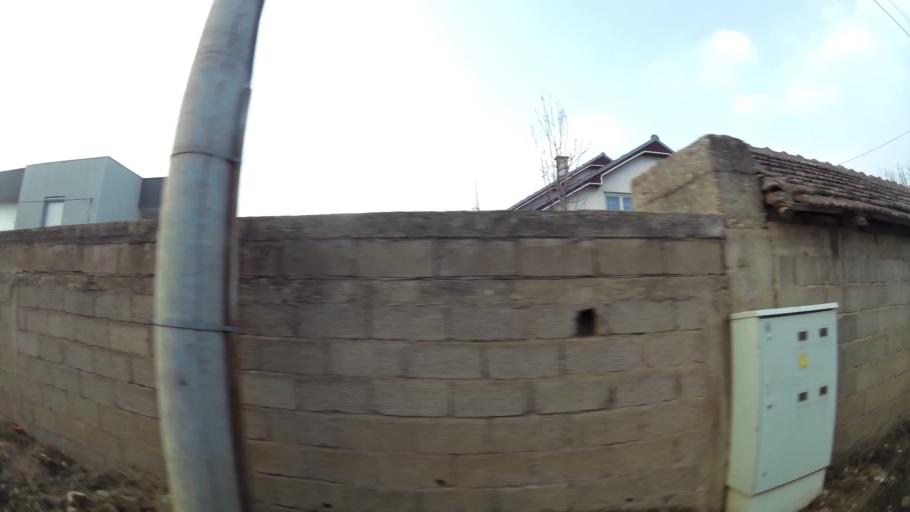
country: MK
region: Aracinovo
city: Arachinovo
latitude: 42.0210
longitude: 21.5632
